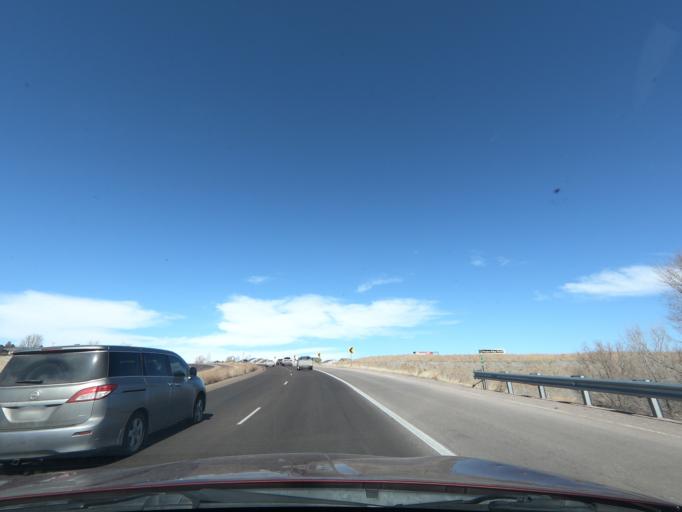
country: US
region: Colorado
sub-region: El Paso County
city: Security-Widefield
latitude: 38.7214
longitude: -104.6821
